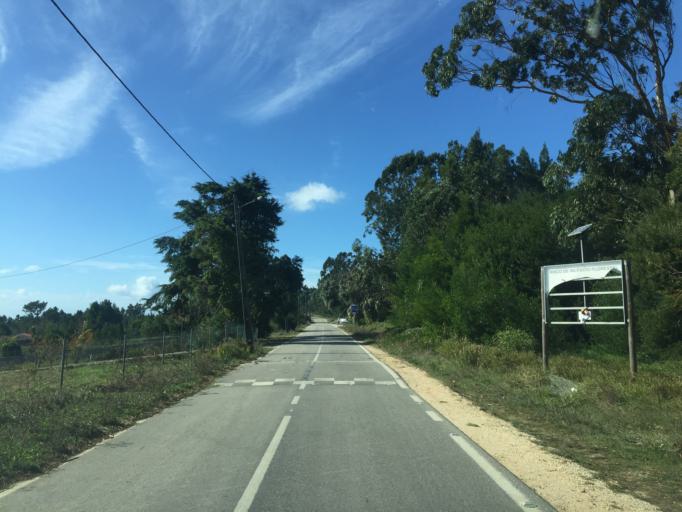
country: PT
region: Coimbra
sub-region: Figueira da Foz
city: Buarcos
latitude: 40.1916
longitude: -8.8724
